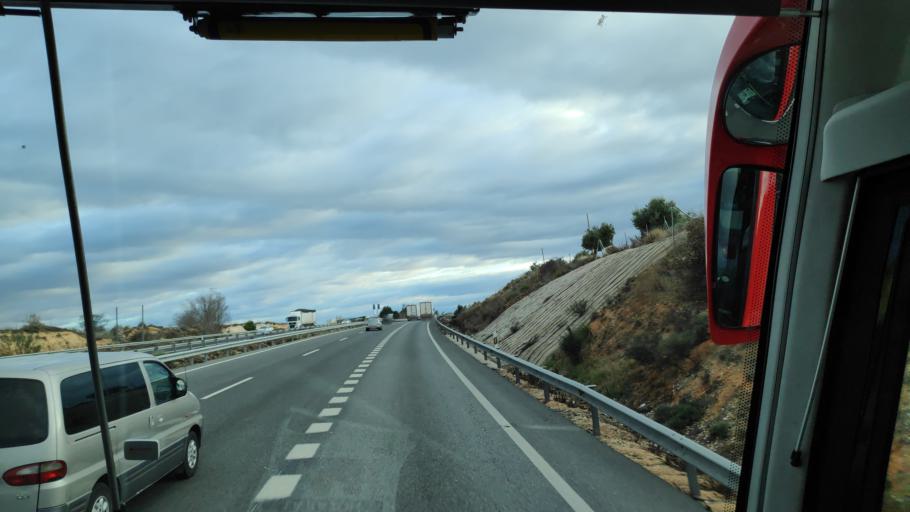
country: ES
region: Madrid
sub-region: Provincia de Madrid
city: Villarejo de Salvanes
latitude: 40.1895
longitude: -3.2992
